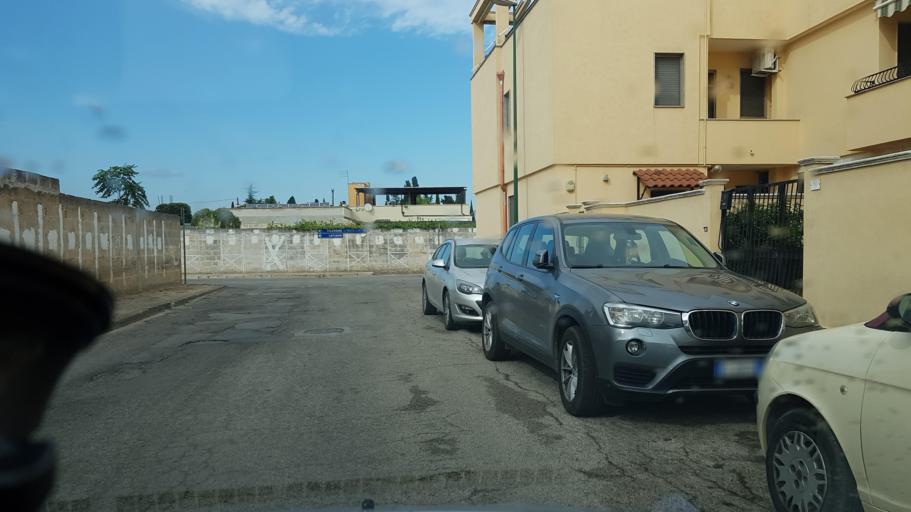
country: IT
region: Apulia
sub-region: Provincia di Brindisi
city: Torre Santa Susanna
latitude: 40.4628
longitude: 17.7465
